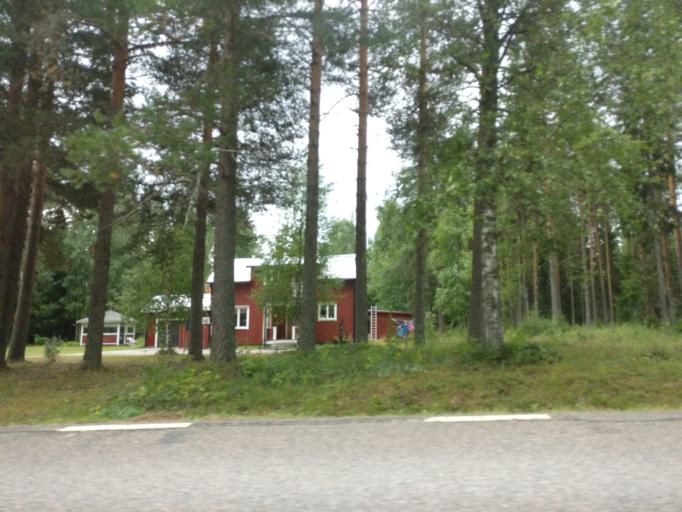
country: SE
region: Vaermland
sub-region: Torsby Kommun
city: Torsby
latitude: 60.7596
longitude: 12.7662
